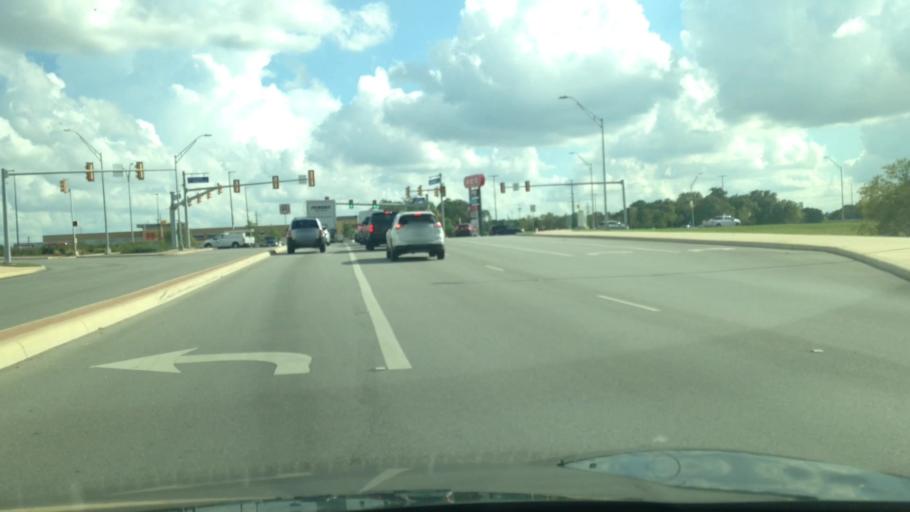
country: US
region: Texas
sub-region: Bexar County
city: Hollywood Park
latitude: 29.5982
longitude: -98.4182
